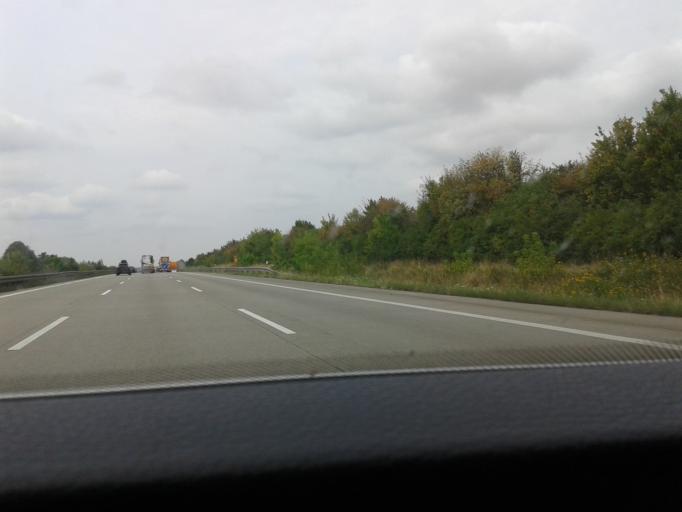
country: DE
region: Saxony-Anhalt
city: Wefensleben
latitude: 52.2045
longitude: 11.1805
